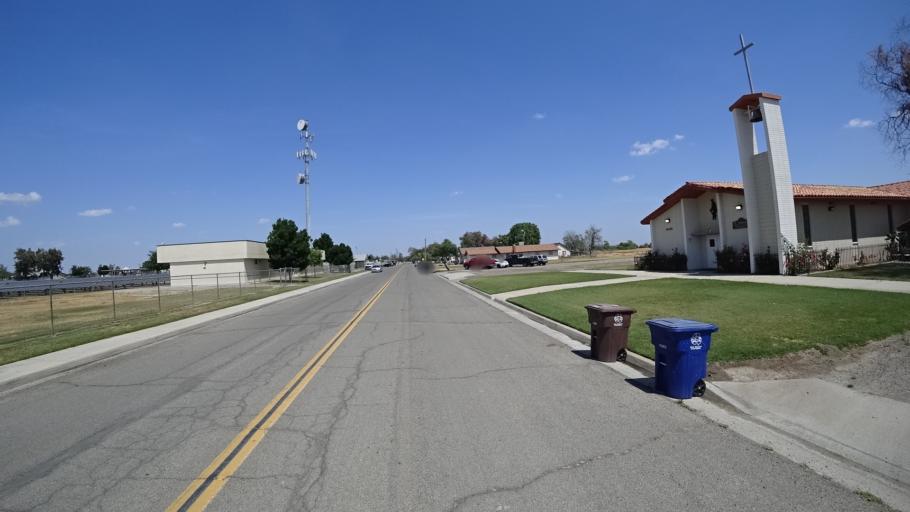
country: US
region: California
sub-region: Kings County
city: Stratford
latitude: 36.1908
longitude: -119.8206
